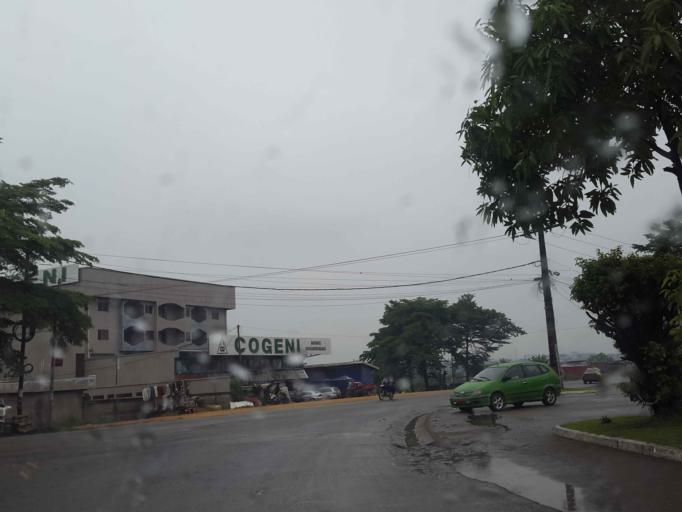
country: CM
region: Littoral
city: Douala
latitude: 4.0853
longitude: 9.7337
